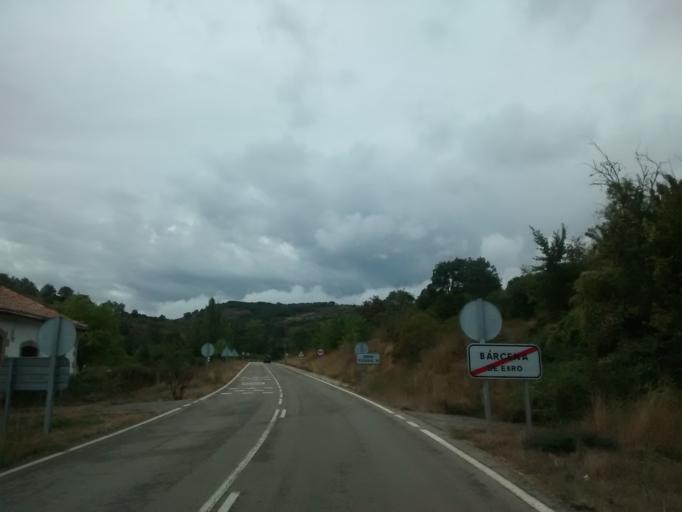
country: ES
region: Castille and Leon
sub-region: Provincia de Palencia
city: Berzosilla
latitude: 42.8533
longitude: -4.0376
